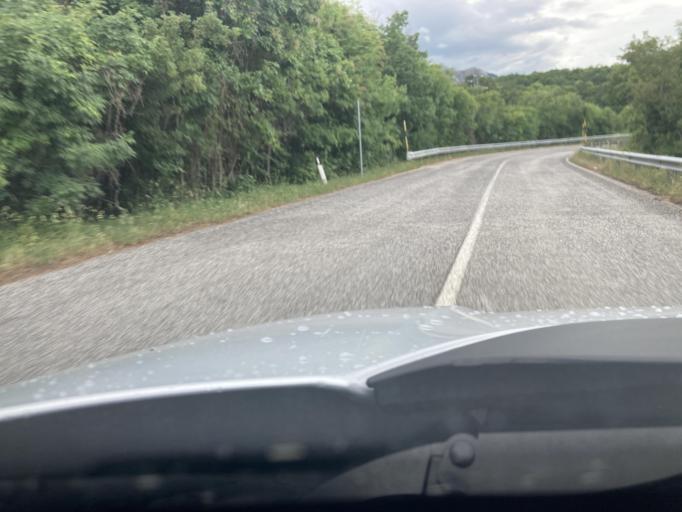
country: IT
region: Abruzzo
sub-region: Provincia dell' Aquila
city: San Panfilo d'Ocre
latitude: 42.2745
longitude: 13.4778
